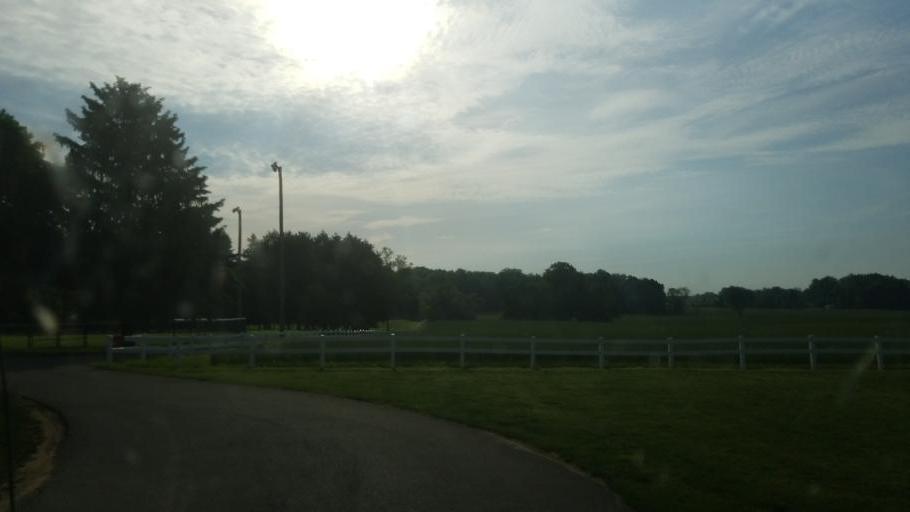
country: US
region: Ohio
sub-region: Wayne County
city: Dalton
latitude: 40.7447
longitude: -81.7431
